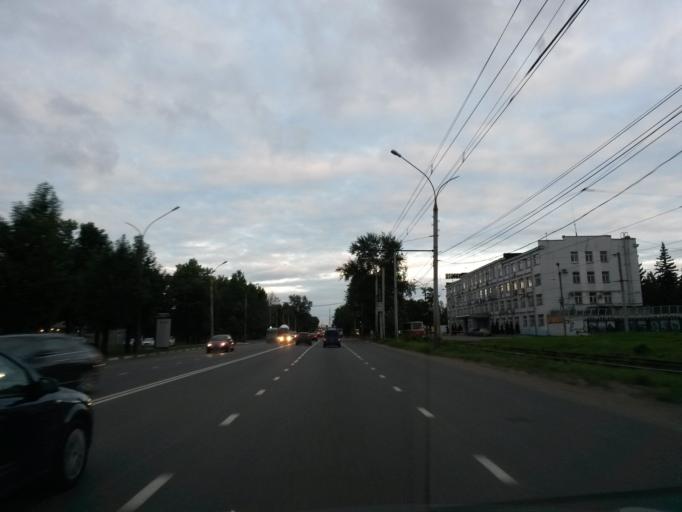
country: RU
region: Jaroslavl
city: Yaroslavl
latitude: 57.6491
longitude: 39.8488
